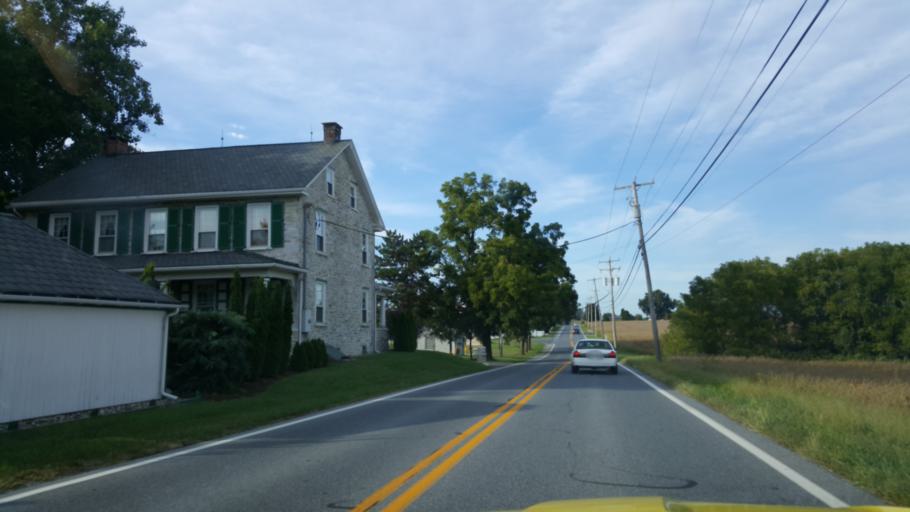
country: US
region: Pennsylvania
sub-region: Lebanon County
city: Palmyra
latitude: 40.3004
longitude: -76.5628
